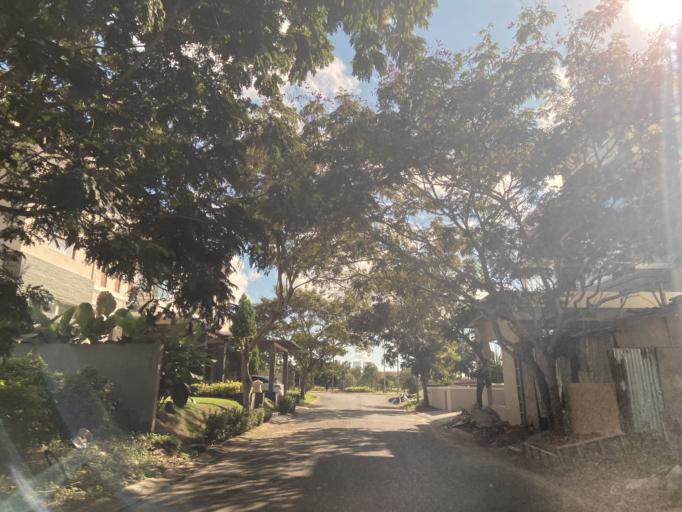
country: SG
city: Singapore
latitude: 1.0942
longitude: 104.0310
